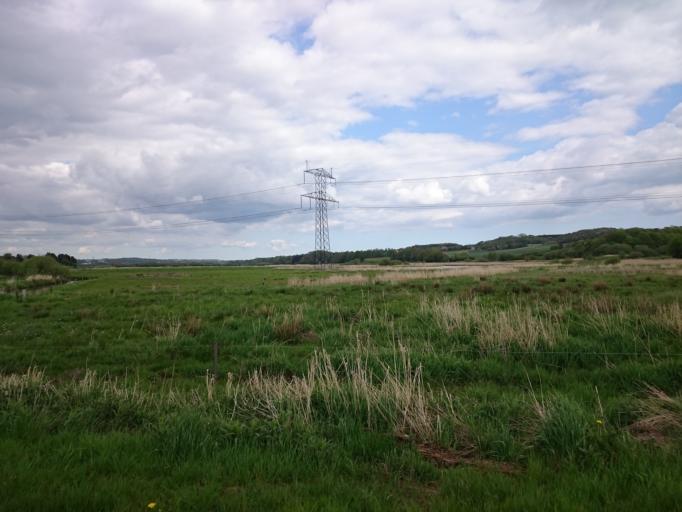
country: DK
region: Central Jutland
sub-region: Arhus Kommune
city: Framlev
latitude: 56.1327
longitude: 10.0405
